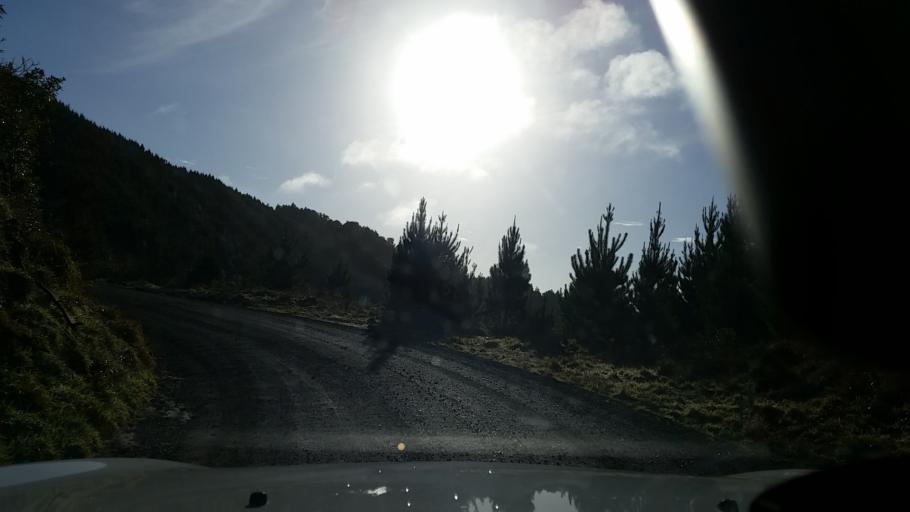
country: NZ
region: Bay of Plenty
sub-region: Kawerau District
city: Kawerau
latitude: -38.0351
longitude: 176.5518
